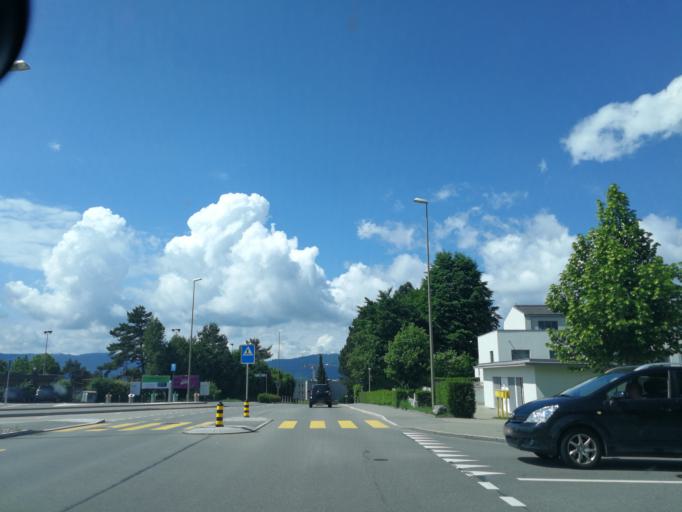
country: CH
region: Zurich
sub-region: Bezirk Meilen
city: Kuesnacht / Itschnach
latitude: 47.3292
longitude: 8.6060
